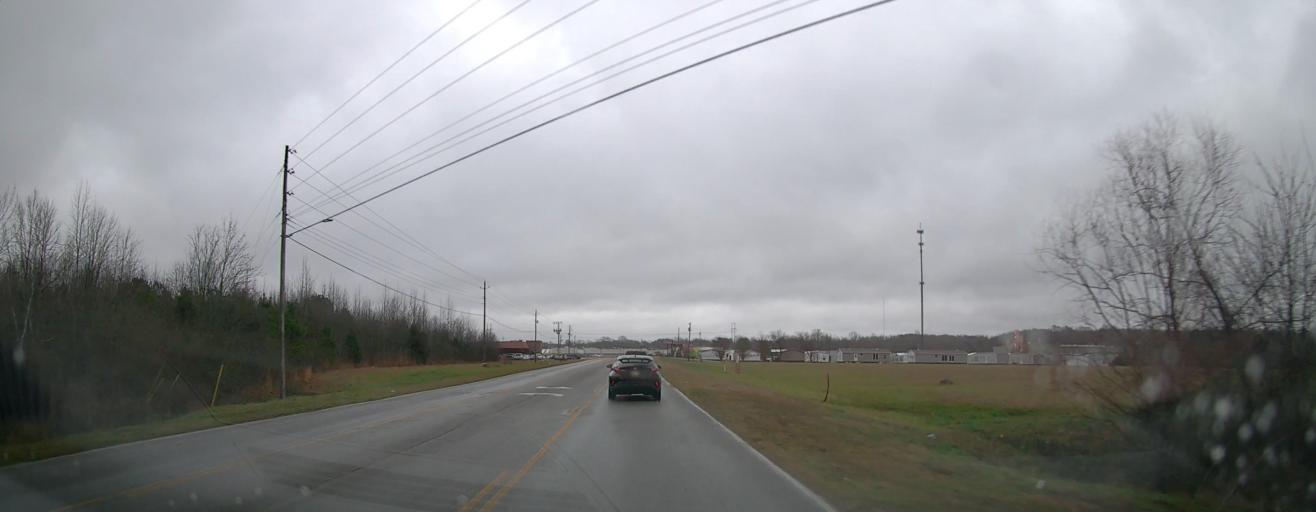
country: US
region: Mississippi
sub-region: Alcorn County
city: Corinth
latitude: 34.9092
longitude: -88.5090
